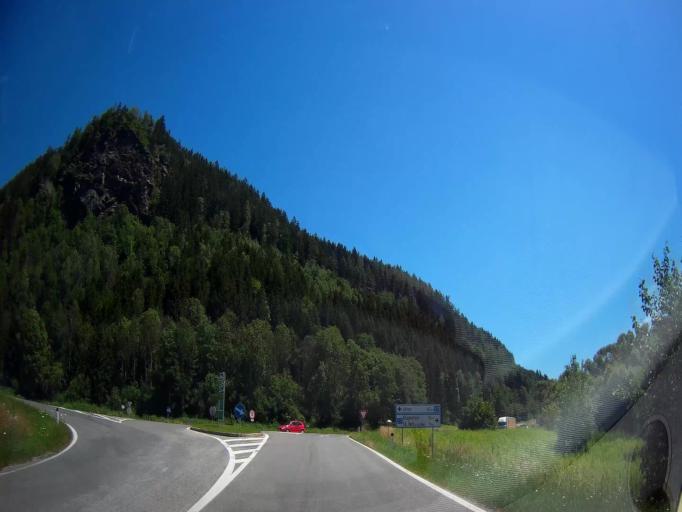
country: AT
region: Carinthia
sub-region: Politischer Bezirk Sankt Veit an der Glan
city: Micheldorf
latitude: 46.9010
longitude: 14.4393
